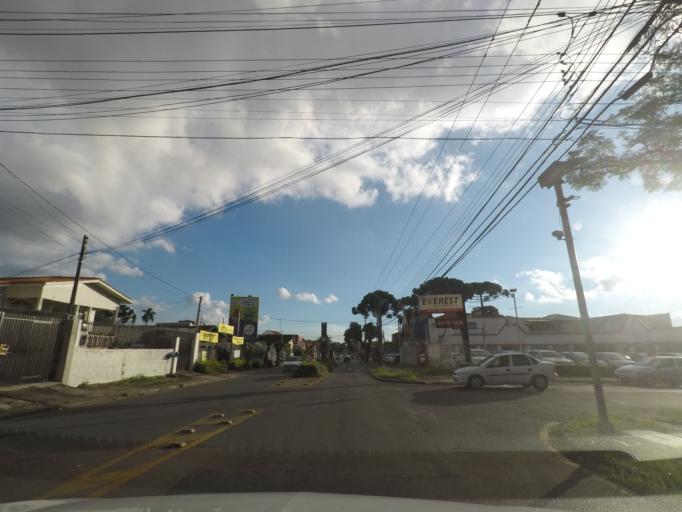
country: BR
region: Parana
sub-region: Sao Jose Dos Pinhais
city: Sao Jose dos Pinhais
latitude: -25.5013
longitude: -49.2543
